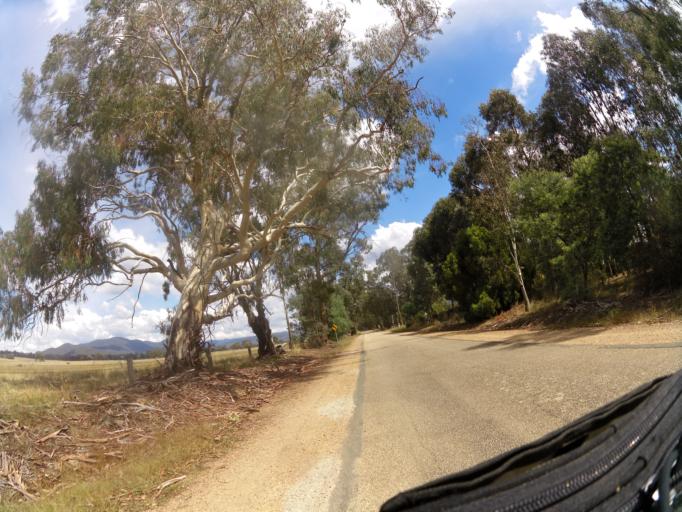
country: AU
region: Victoria
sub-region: Benalla
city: Benalla
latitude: -36.7521
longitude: 145.9812
